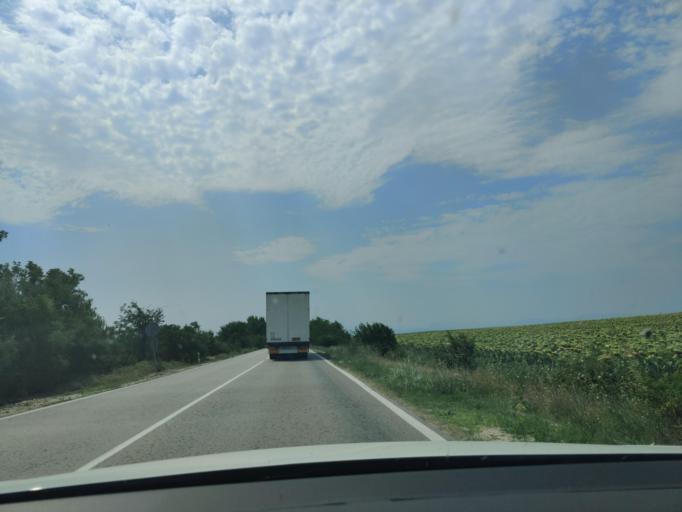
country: BG
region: Vidin
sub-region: Obshtina Vidin
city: Dunavtsi
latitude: 43.8627
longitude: 22.7820
